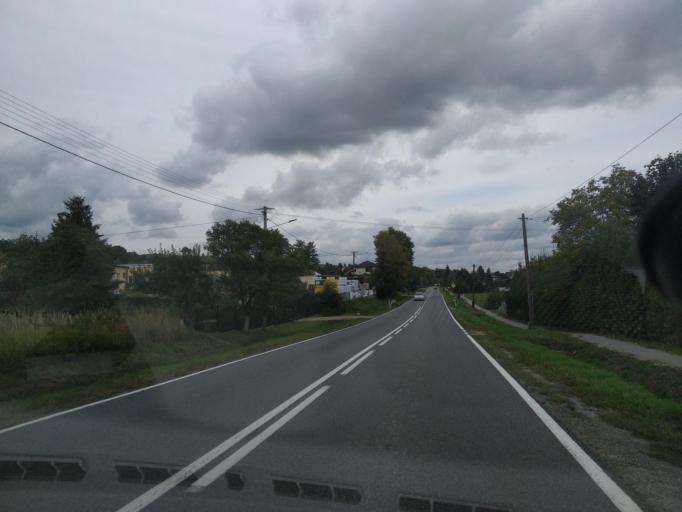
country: PL
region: Lesser Poland Voivodeship
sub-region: Powiat gorlicki
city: Sekowa
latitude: 49.6118
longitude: 21.2072
